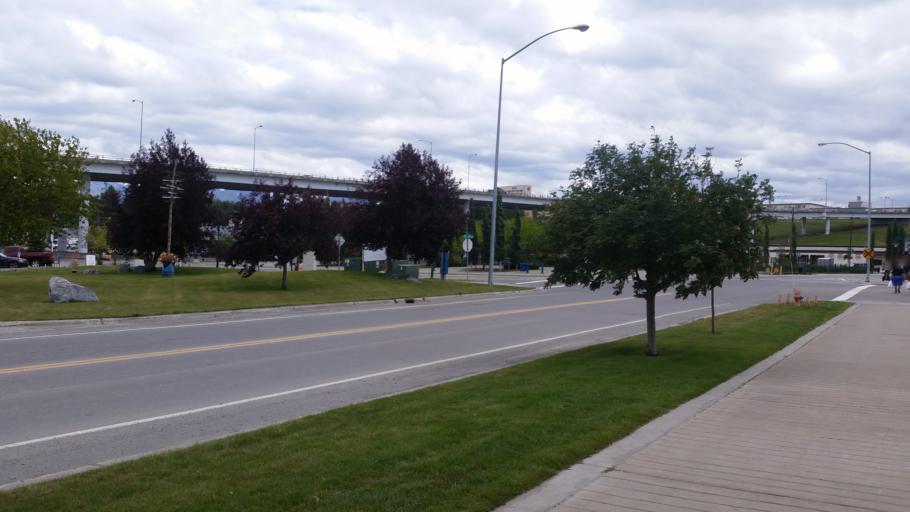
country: US
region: Alaska
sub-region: Anchorage Municipality
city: Anchorage
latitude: 61.2229
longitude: -149.8877
